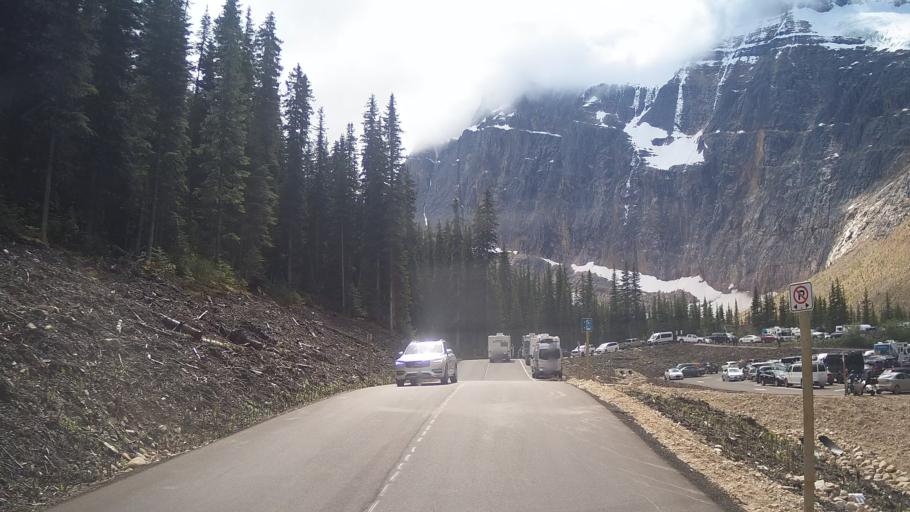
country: CA
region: Alberta
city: Jasper Park Lodge
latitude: 52.6887
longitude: -118.0559
